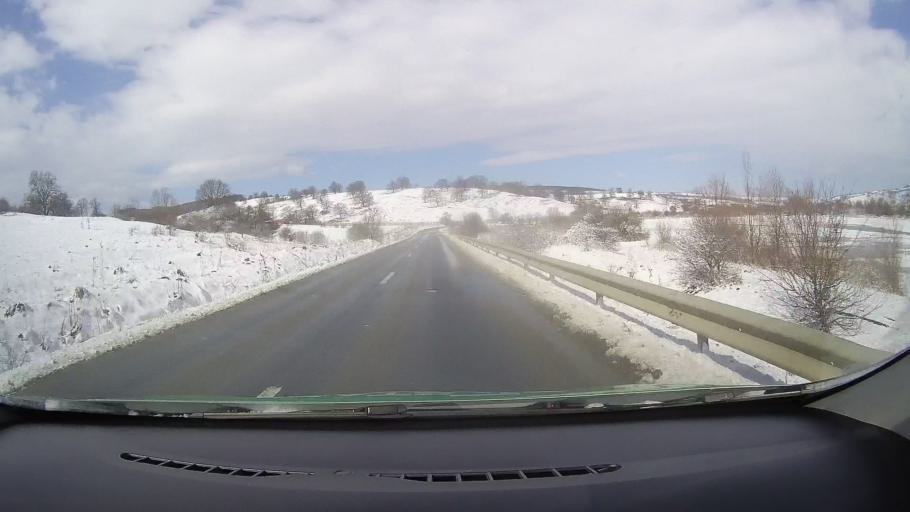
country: RO
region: Sibiu
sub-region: Comuna Altina
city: Altina
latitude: 45.9451
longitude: 24.4517
